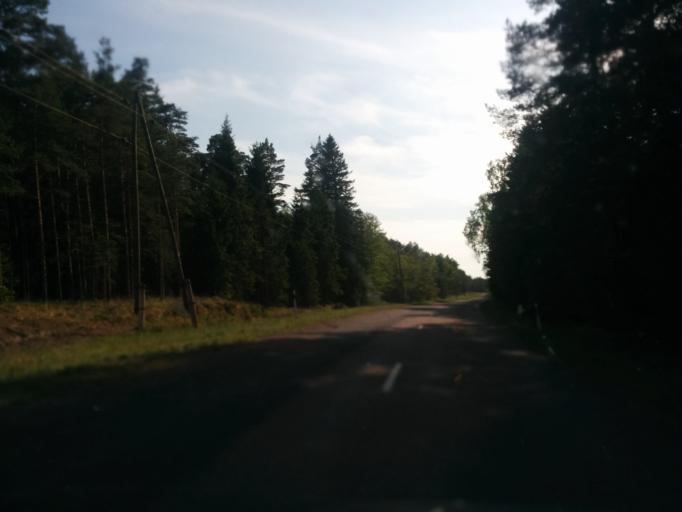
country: LV
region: Dundaga
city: Dundaga
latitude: 57.6641
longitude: 22.3008
